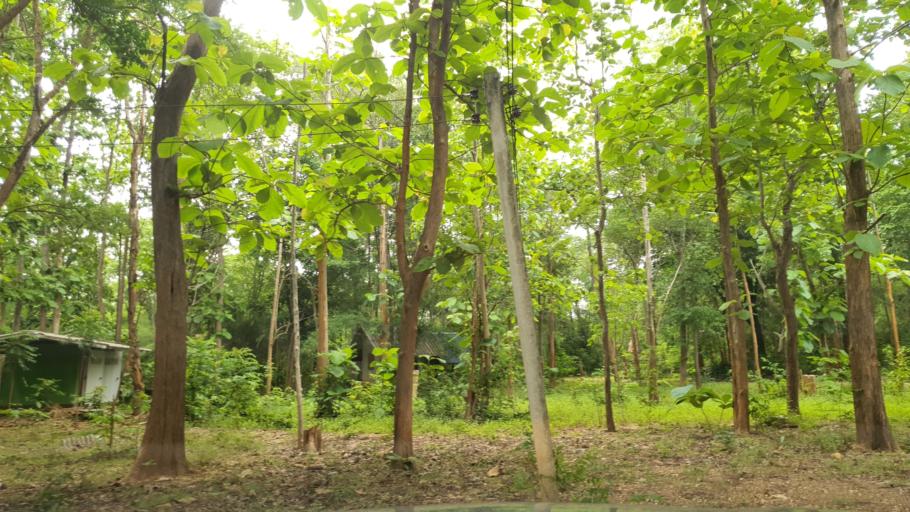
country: TH
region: Sukhothai
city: Thung Saliam
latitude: 17.2385
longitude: 99.5430
